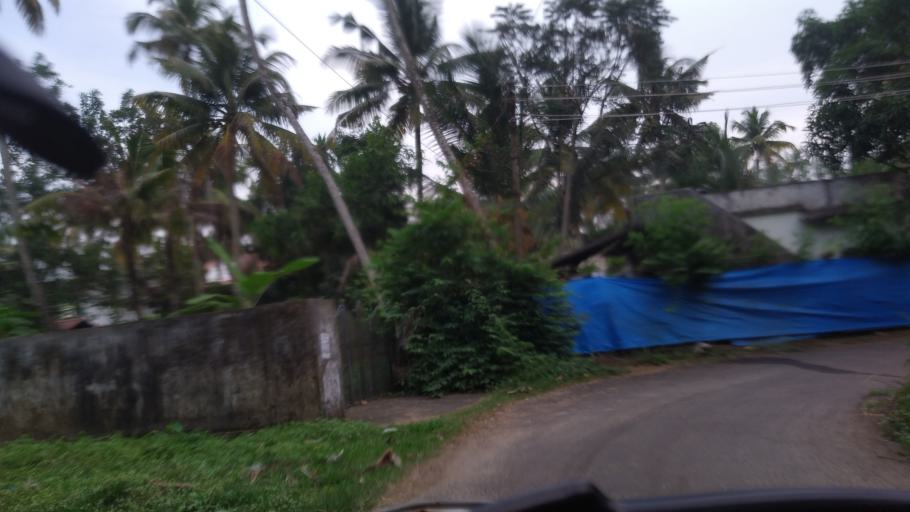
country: IN
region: Kerala
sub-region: Thrissur District
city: Kodungallur
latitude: 10.1359
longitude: 76.2000
